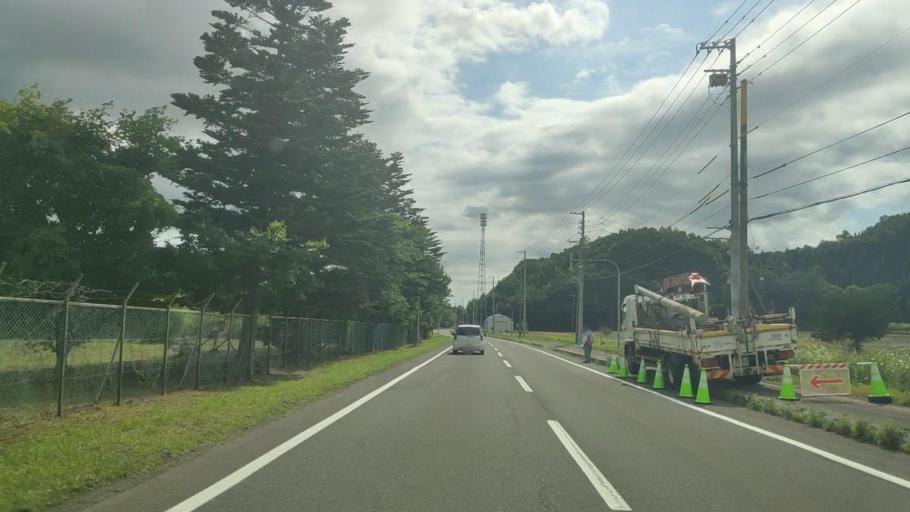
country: JP
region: Hokkaido
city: Date
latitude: 42.5705
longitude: 140.9254
